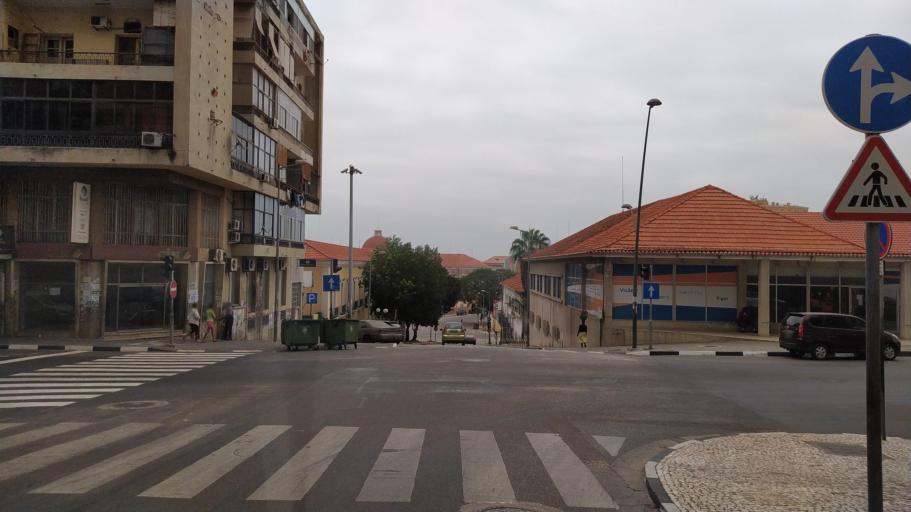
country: AO
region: Luanda
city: Luanda
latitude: -8.8143
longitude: 13.2348
